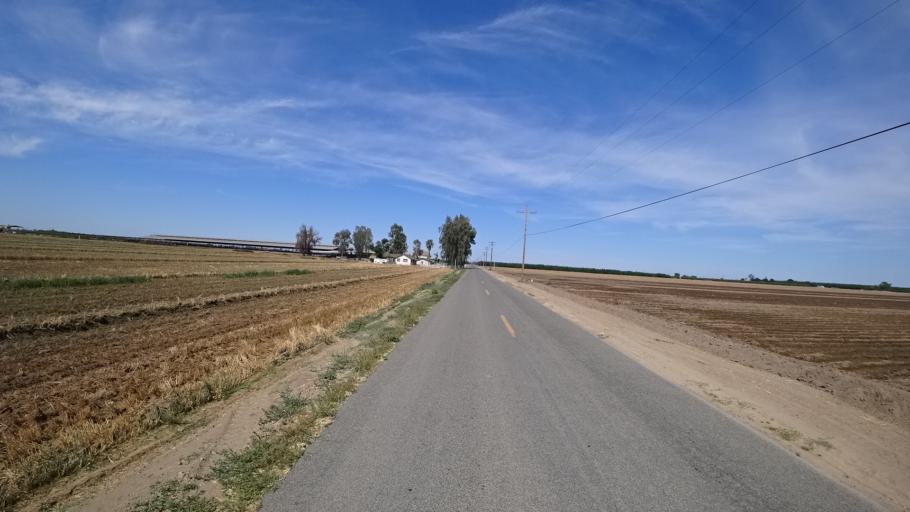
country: US
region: California
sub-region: Kings County
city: Hanford
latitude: 36.3573
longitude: -119.5722
